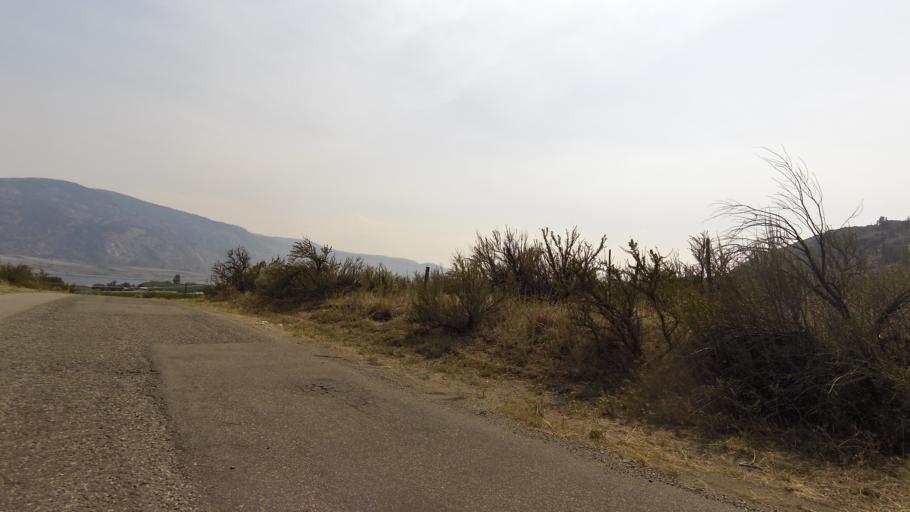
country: CA
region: British Columbia
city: Osoyoos
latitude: 49.0542
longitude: -119.5158
